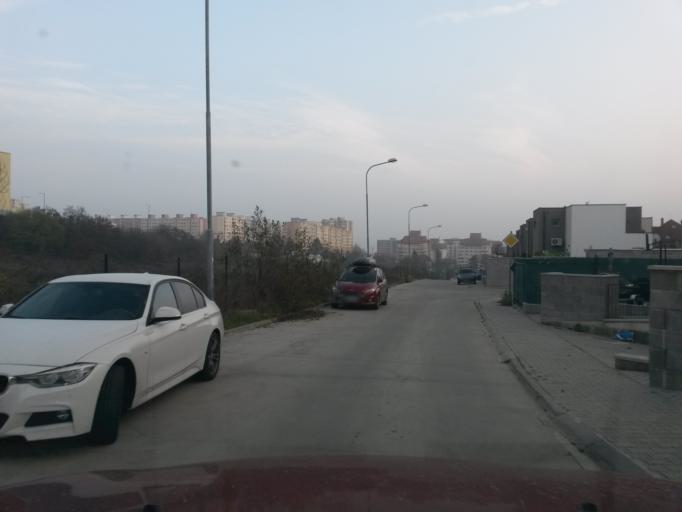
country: SK
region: Kosicky
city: Kosice
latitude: 48.7173
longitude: 21.2035
